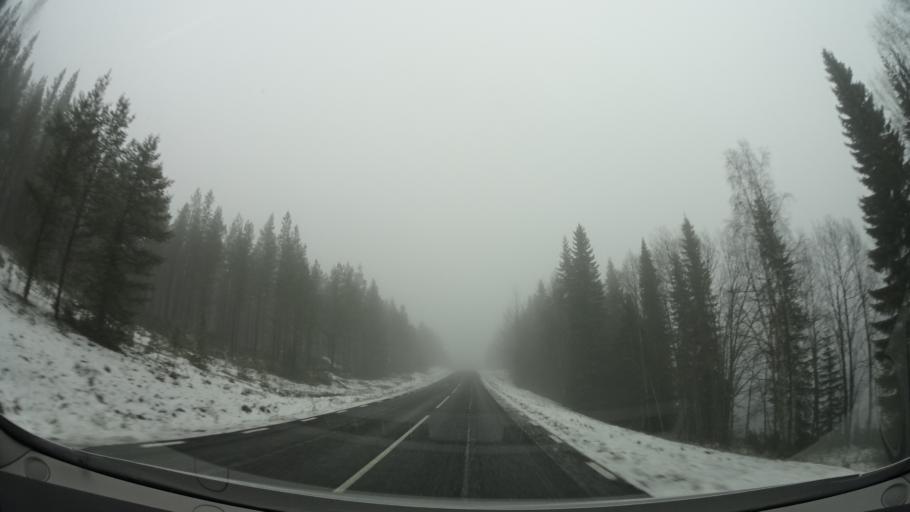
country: SE
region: Vaesterbotten
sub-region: Asele Kommun
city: Insjon
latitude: 64.3499
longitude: 17.8409
